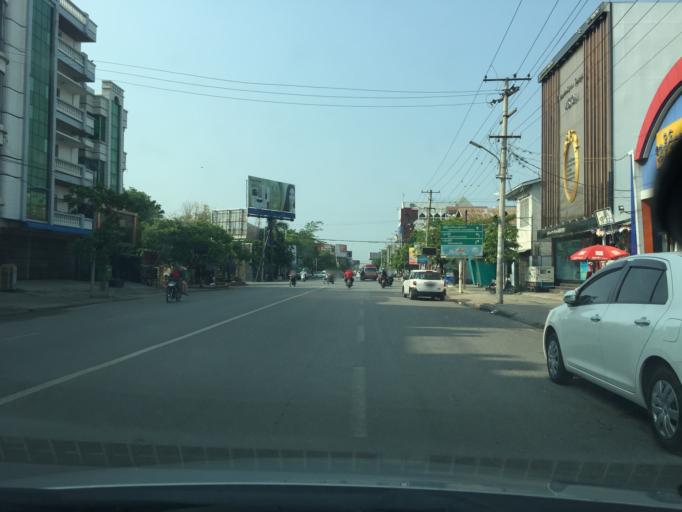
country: MM
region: Mandalay
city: Mandalay
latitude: 21.9730
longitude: 96.0838
